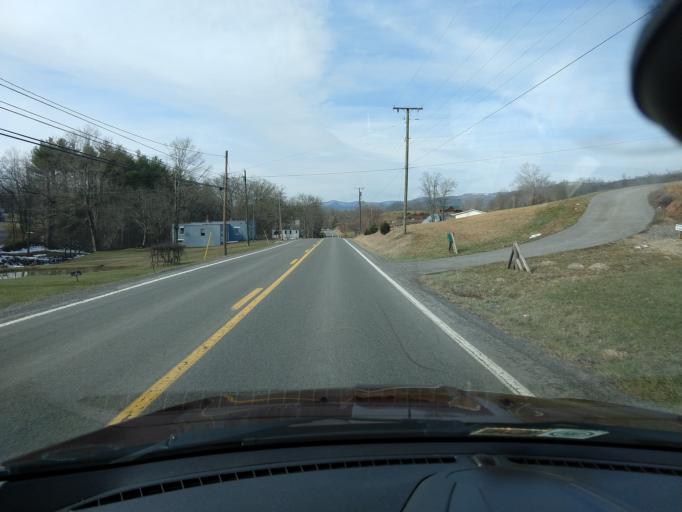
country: US
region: West Virginia
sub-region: Pocahontas County
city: Marlinton
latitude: 38.1646
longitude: -80.1625
